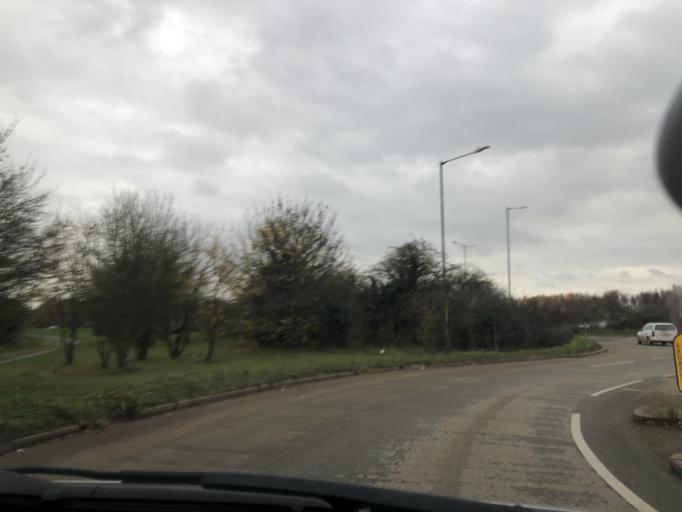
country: GB
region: England
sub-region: Kent
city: Dartford
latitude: 51.4391
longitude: 0.1851
